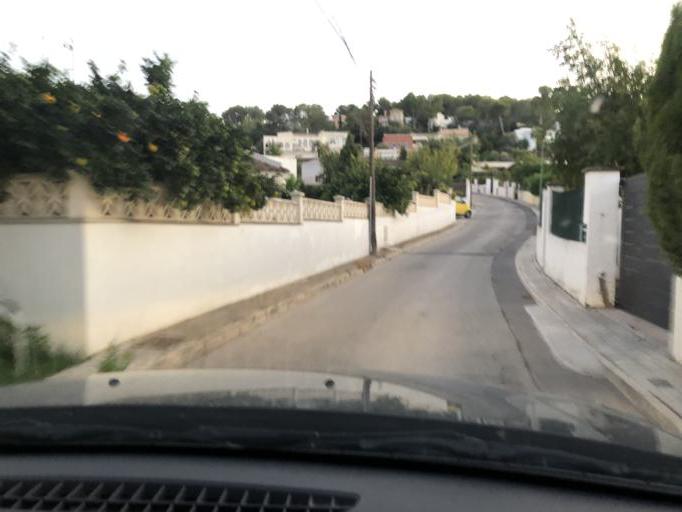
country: ES
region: Balearic Islands
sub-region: Illes Balears
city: Santa Ponsa
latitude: 39.5251
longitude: 2.4825
